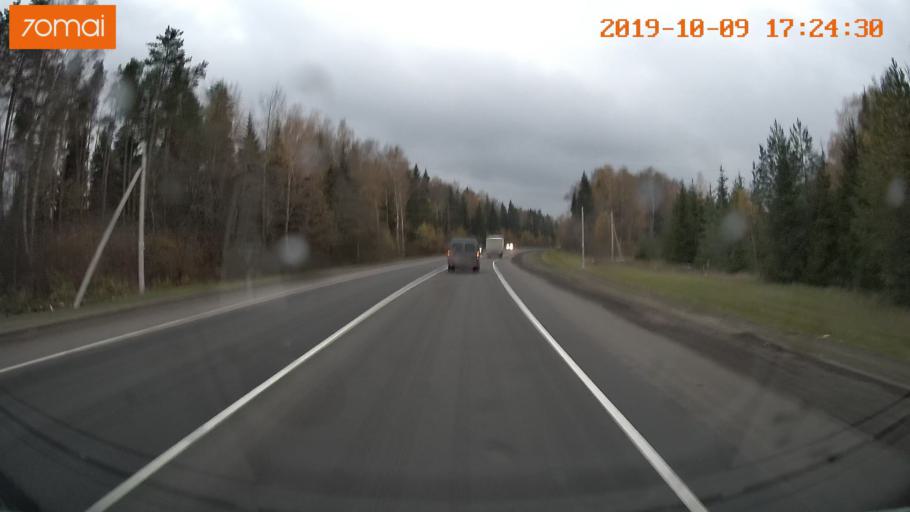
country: RU
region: Ivanovo
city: Furmanov
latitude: 57.1849
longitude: 41.1062
